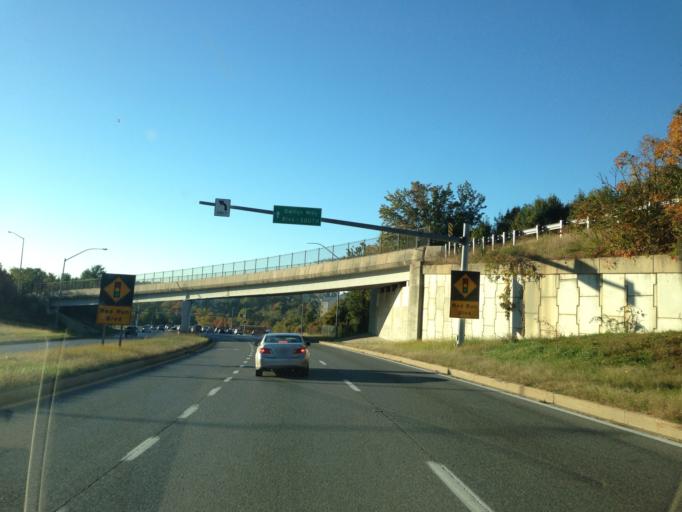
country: US
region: Maryland
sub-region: Baltimore County
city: Owings Mills
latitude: 39.4058
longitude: -76.7969
